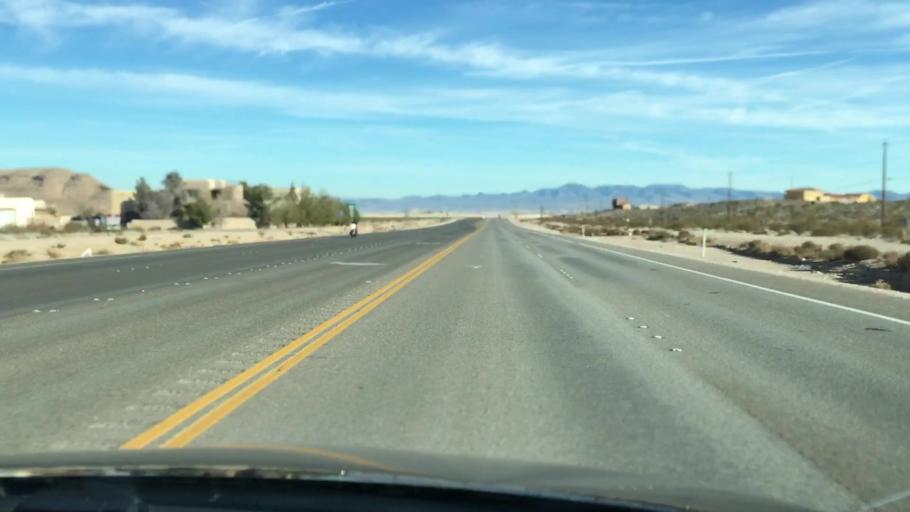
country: US
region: Nevada
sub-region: Clark County
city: Summerlin South
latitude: 36.0326
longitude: -115.3438
